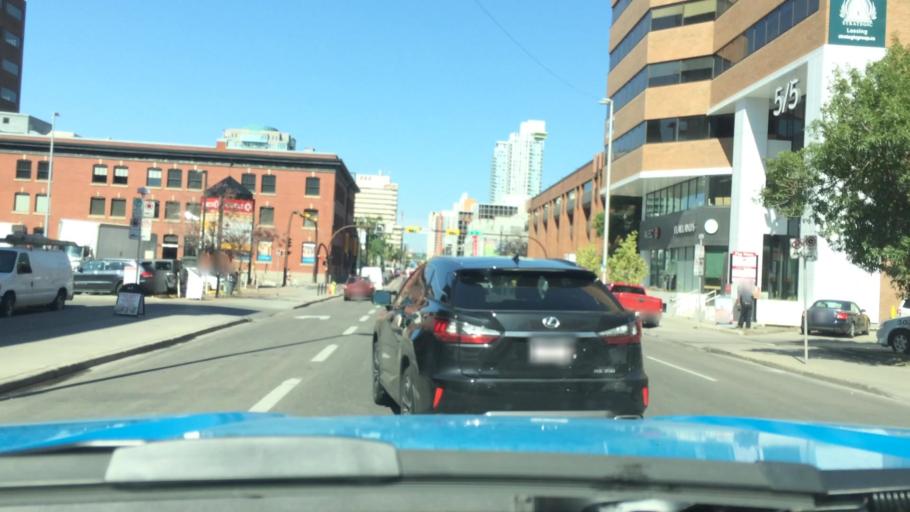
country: CA
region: Alberta
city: Calgary
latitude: 51.0427
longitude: -114.0731
